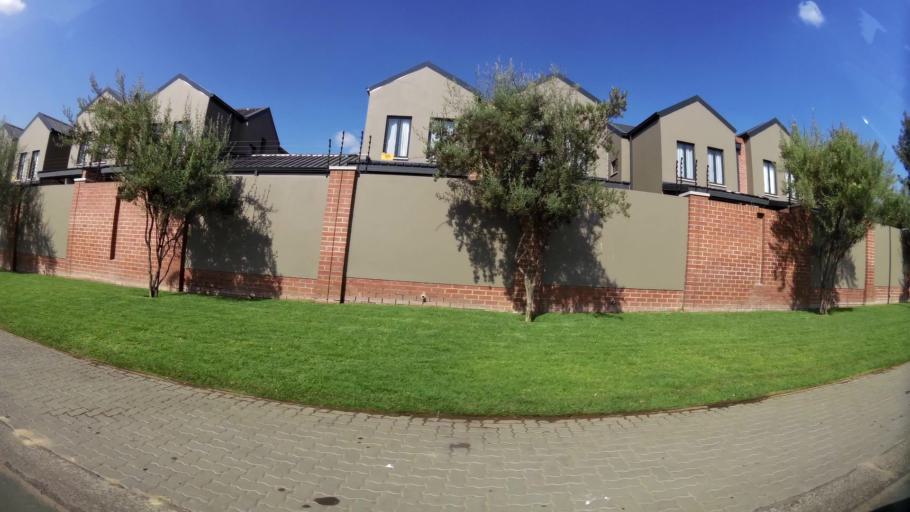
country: ZA
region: Gauteng
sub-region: City of Johannesburg Metropolitan Municipality
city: Modderfontein
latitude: -26.0796
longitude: 28.2454
